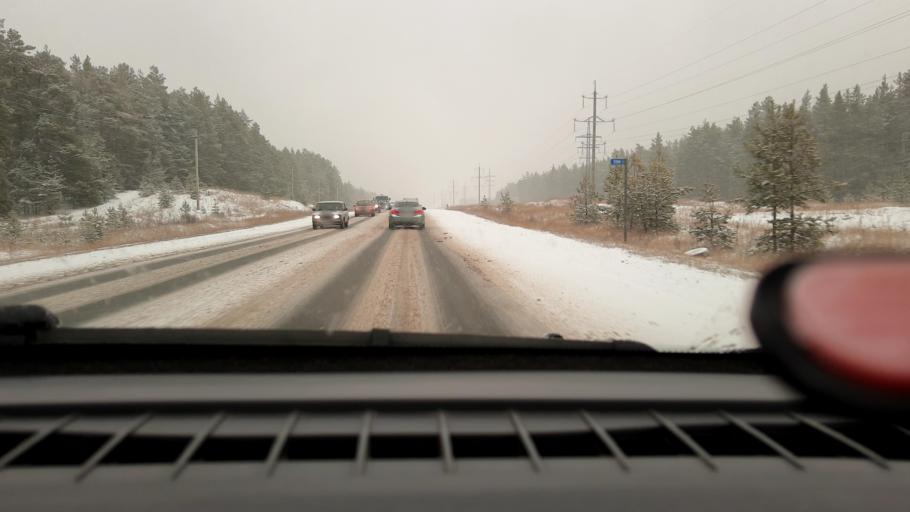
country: RU
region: Nizjnij Novgorod
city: Lukino
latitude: 56.3966
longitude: 43.6743
